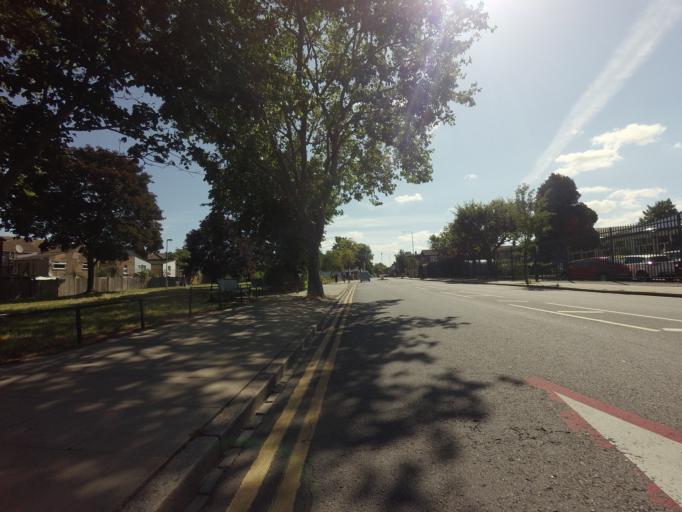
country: GB
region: England
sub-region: Greater London
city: Poplar
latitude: 51.5372
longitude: 0.0104
